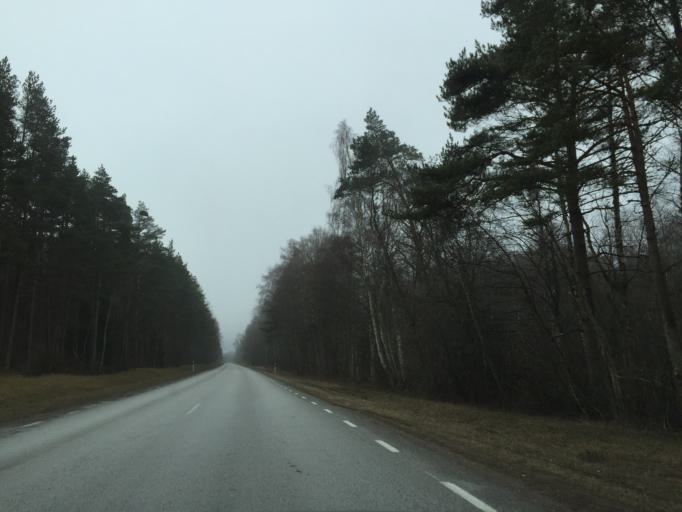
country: EE
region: Saare
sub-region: Kuressaare linn
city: Kuressaare
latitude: 58.1912
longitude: 22.2679
